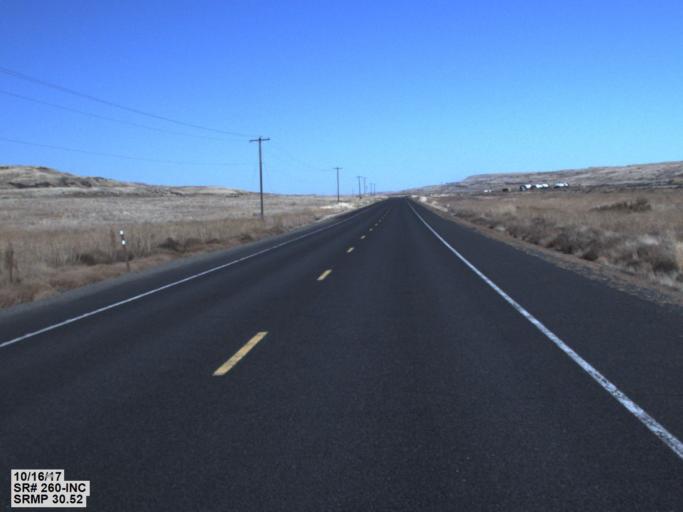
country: US
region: Washington
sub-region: Franklin County
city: Connell
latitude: 46.6782
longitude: -118.4539
